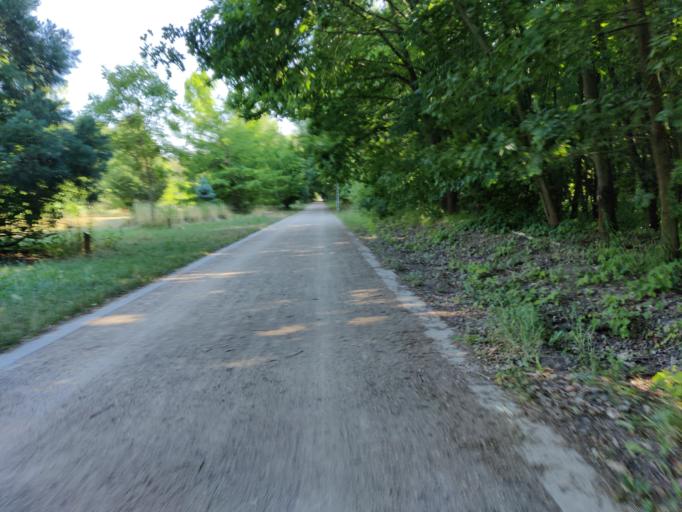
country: DE
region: Saxony
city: Markkleeberg
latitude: 51.2874
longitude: 12.3517
